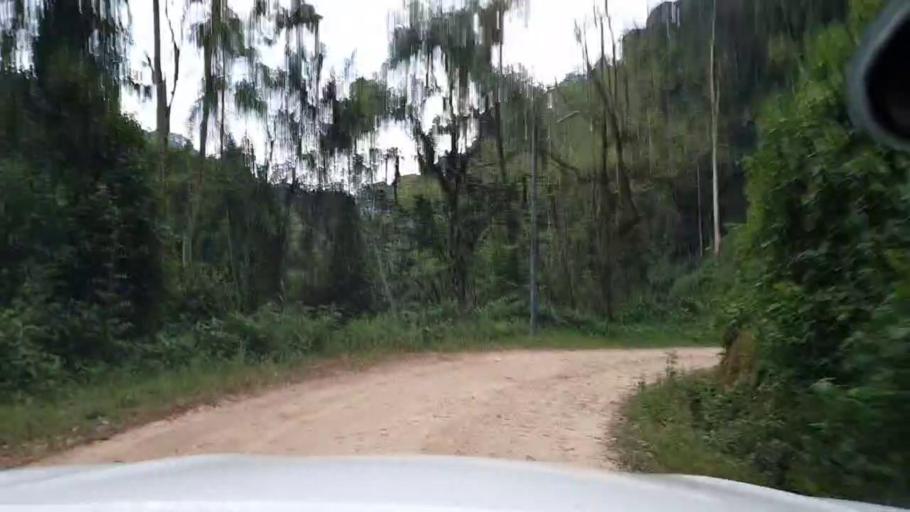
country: RW
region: Western Province
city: Cyangugu
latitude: -2.5565
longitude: 29.2322
